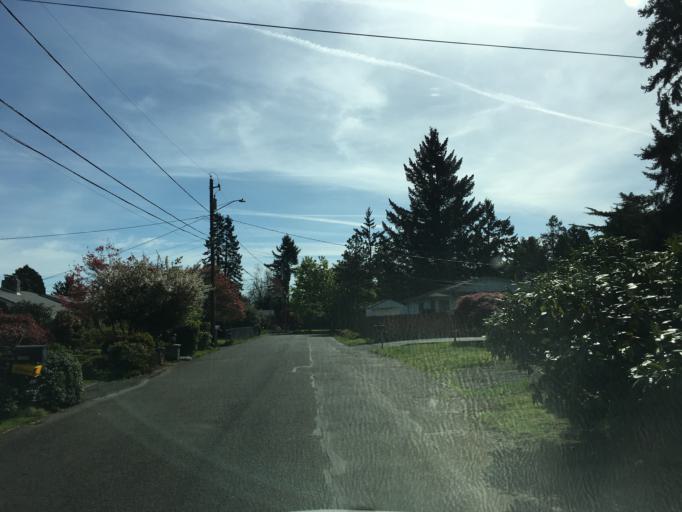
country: US
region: Oregon
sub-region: Multnomah County
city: Lents
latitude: 45.5387
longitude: -122.5255
